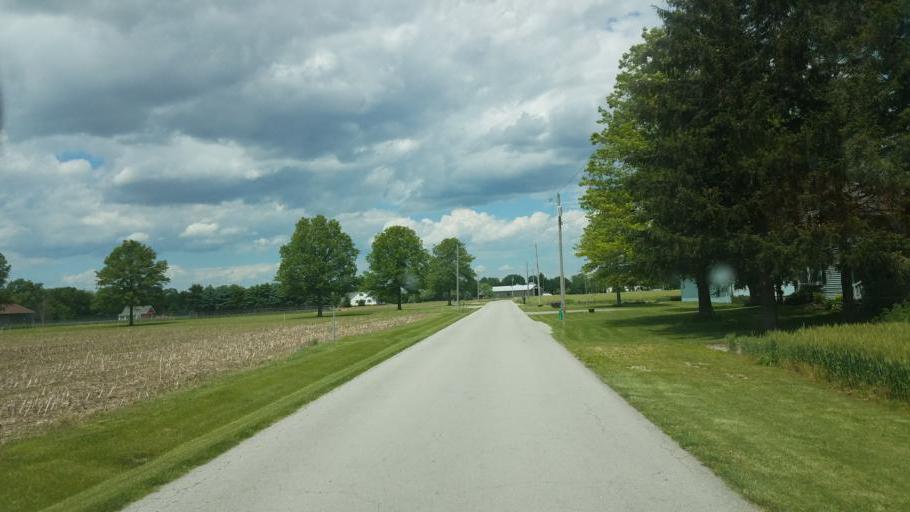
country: US
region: Ohio
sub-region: Huron County
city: Monroeville
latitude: 41.2698
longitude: -82.6777
